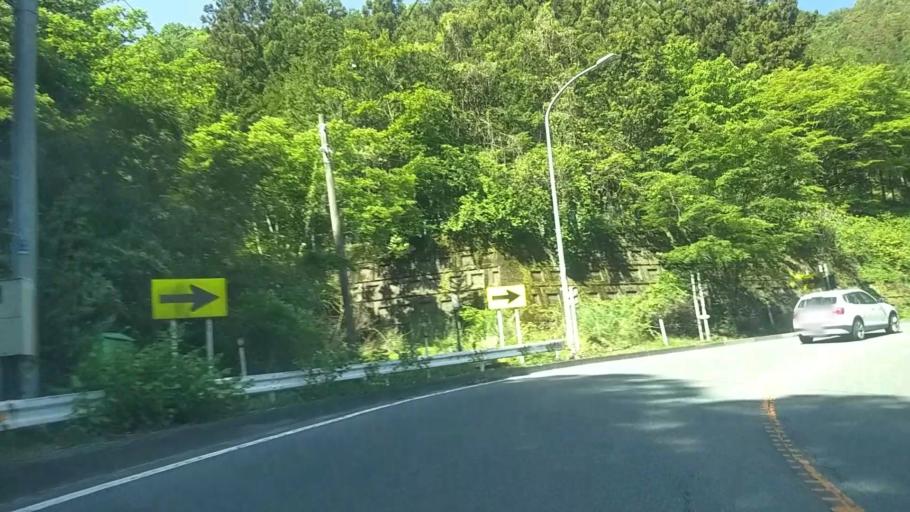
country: JP
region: Shizuoka
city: Fujinomiya
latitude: 35.3205
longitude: 138.4369
